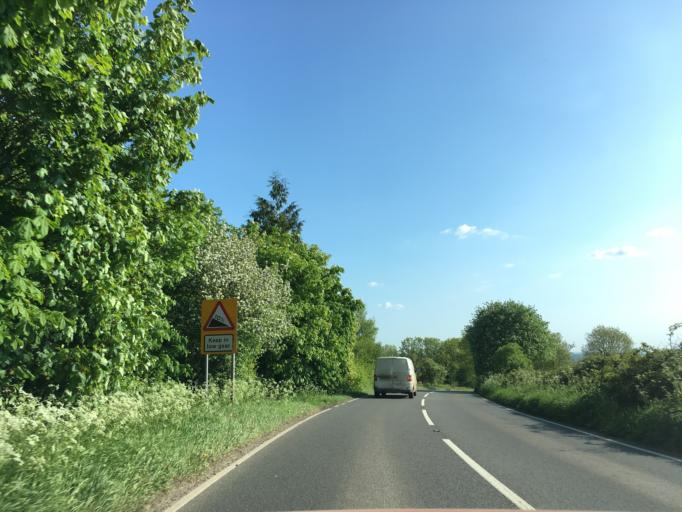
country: GB
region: England
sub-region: Gloucestershire
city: Wotton-under-Edge
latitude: 51.6501
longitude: -2.3356
